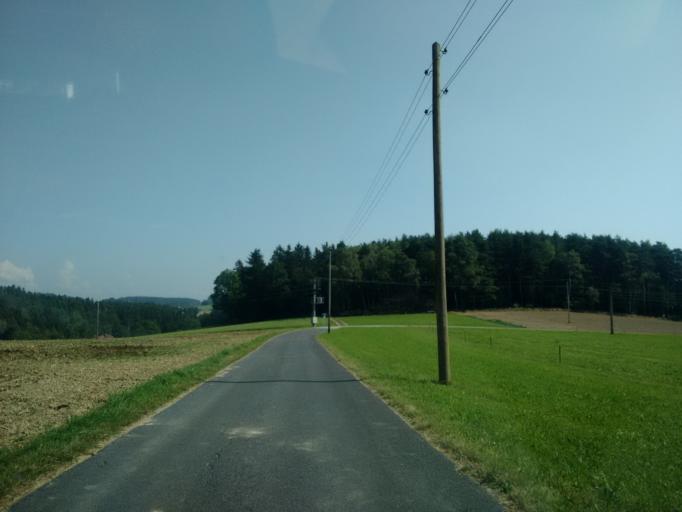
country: AT
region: Upper Austria
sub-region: Politischer Bezirk Urfahr-Umgebung
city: Haibach im Muhlkreis
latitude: 48.4110
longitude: 14.3552
